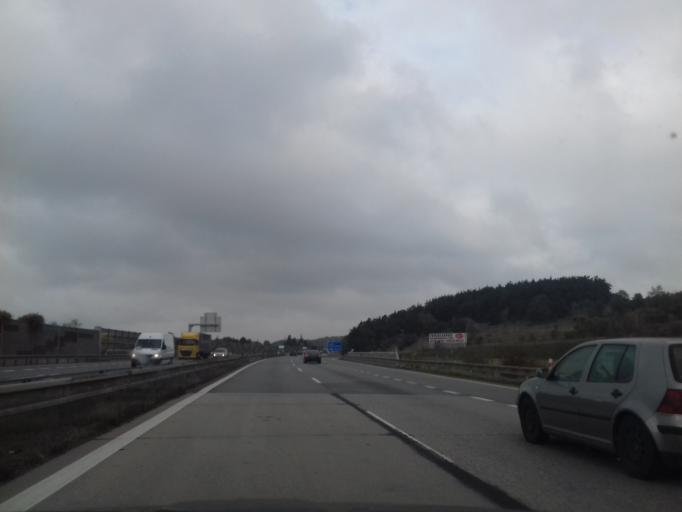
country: CZ
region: Vysocina
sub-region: Okres Zd'ar nad Sazavou
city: Velke Mezirici
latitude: 49.3468
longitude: 16.0416
